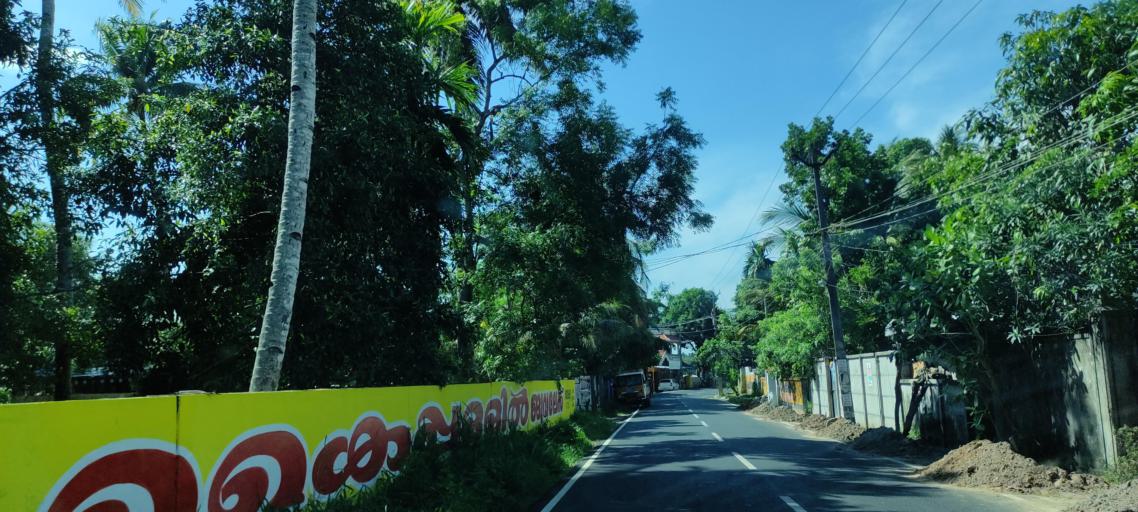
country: IN
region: Kerala
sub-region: Alappuzha
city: Mavelikara
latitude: 9.3101
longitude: 76.3842
